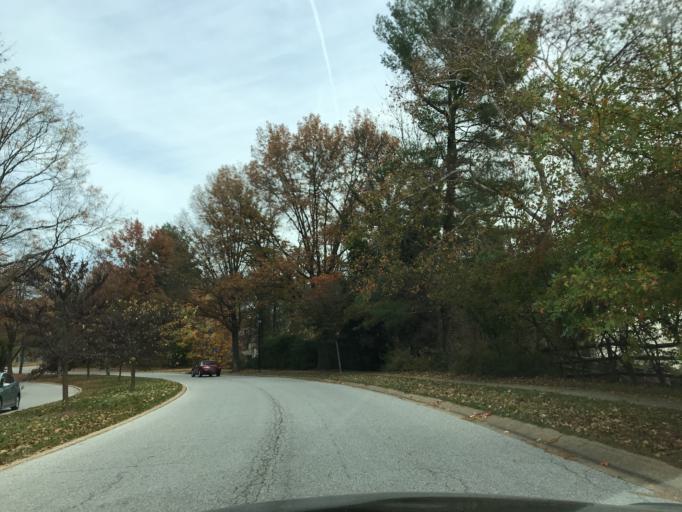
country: US
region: Maryland
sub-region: Howard County
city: Columbia
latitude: 39.2240
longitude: -76.8838
